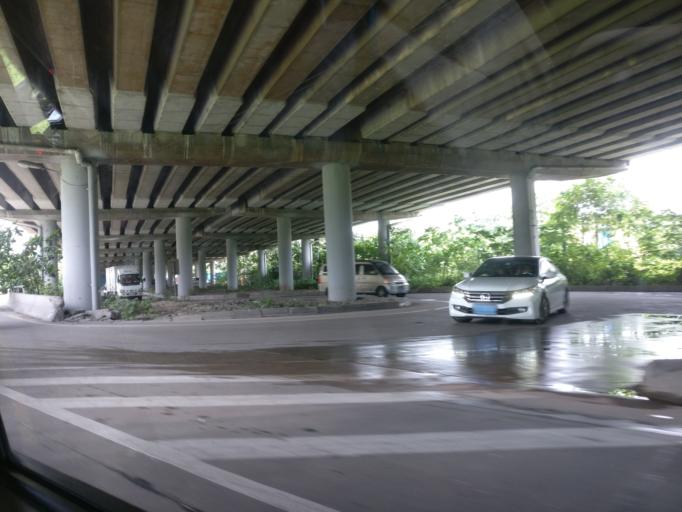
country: CN
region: Guangdong
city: Luopu
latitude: 23.0633
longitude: 113.3003
